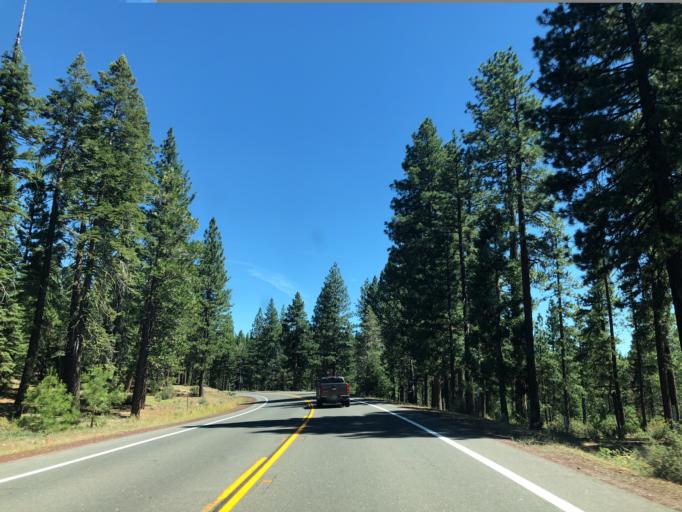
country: US
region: California
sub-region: Lassen County
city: Susanville
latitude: 40.4194
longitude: -120.7851
